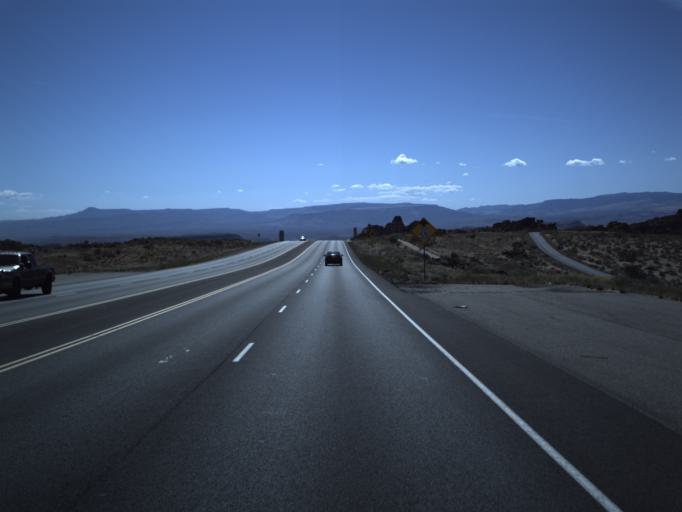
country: US
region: Utah
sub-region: Washington County
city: Santa Clara
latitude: 37.1771
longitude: -113.6190
